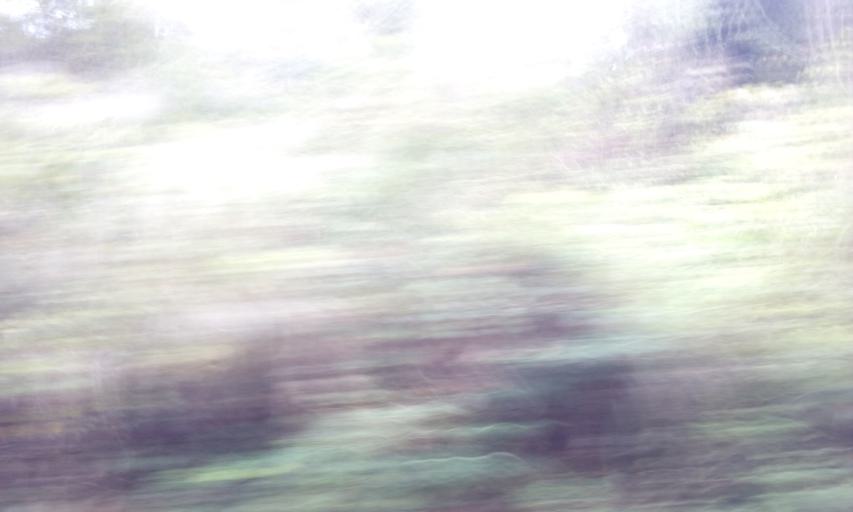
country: TH
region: Trat
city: Laem Ngop
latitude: 12.2657
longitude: 102.3050
